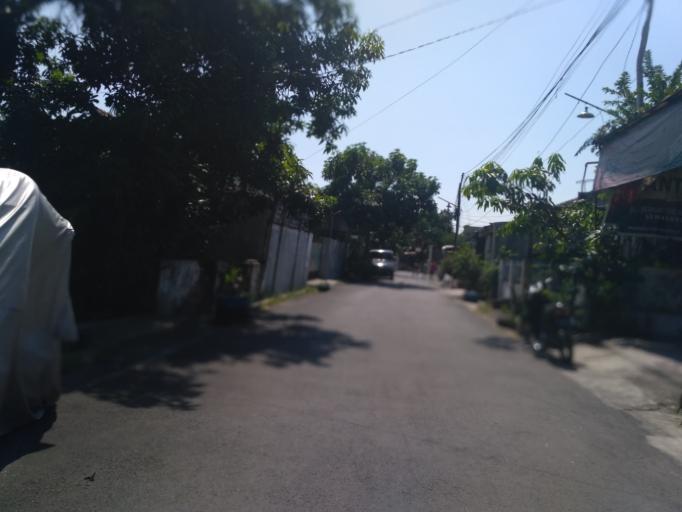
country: ID
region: Central Java
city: Semarang
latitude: -7.0037
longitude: 110.4406
